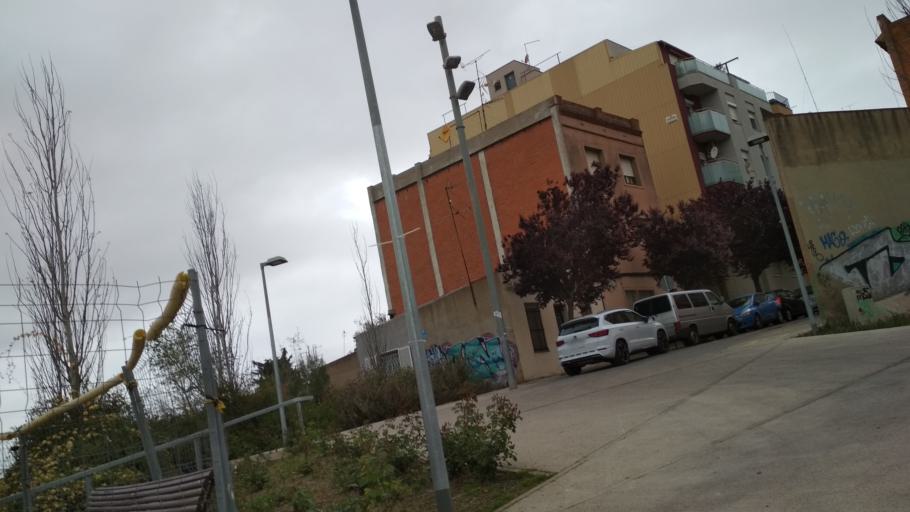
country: ES
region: Catalonia
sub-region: Provincia de Barcelona
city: L'Hospitalet de Llobregat
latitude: 41.3636
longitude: 2.0954
